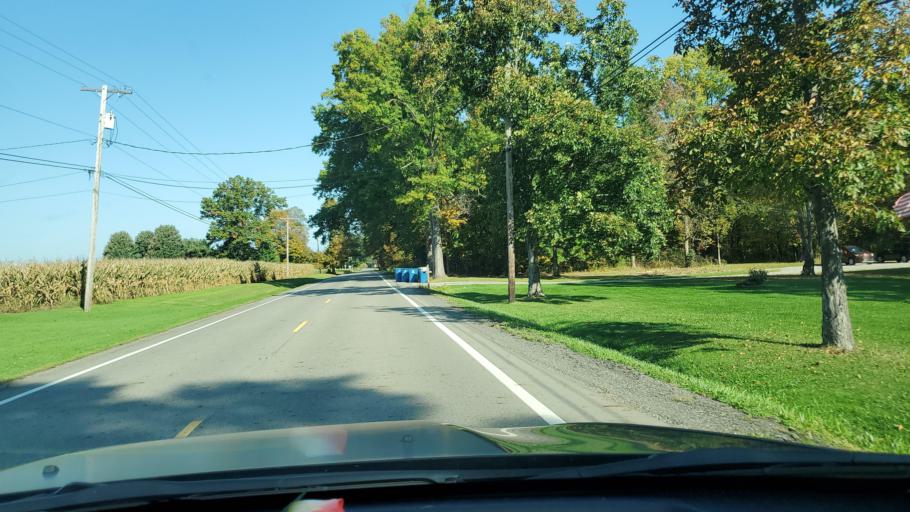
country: US
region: Ohio
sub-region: Trumbull County
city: Brookfield Center
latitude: 41.4022
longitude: -80.5719
